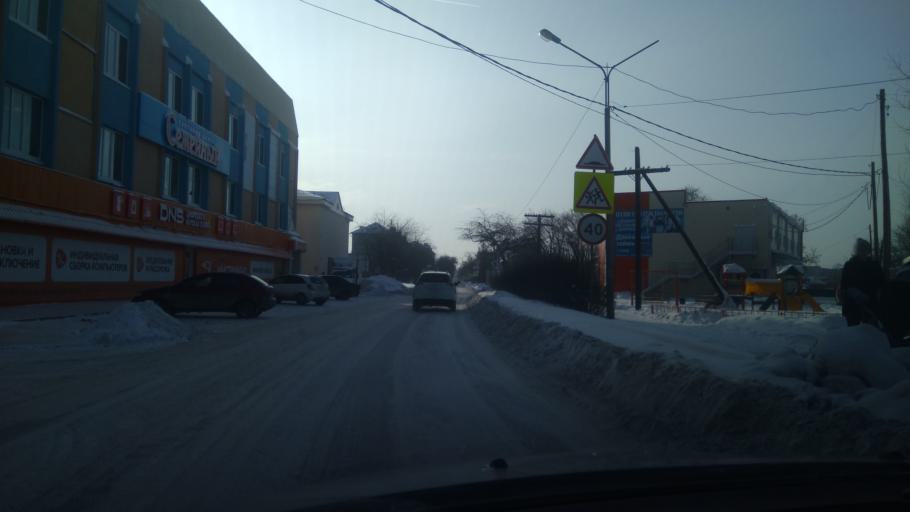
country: RU
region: Sverdlovsk
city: Sukhoy Log
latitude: 56.9061
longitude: 62.0332
